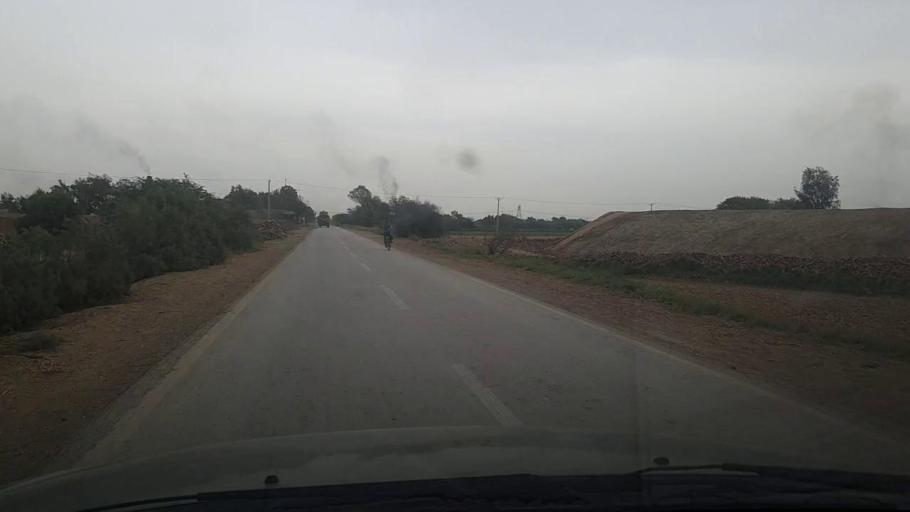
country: PK
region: Sindh
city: Daulatpur
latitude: 26.3379
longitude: 68.1206
